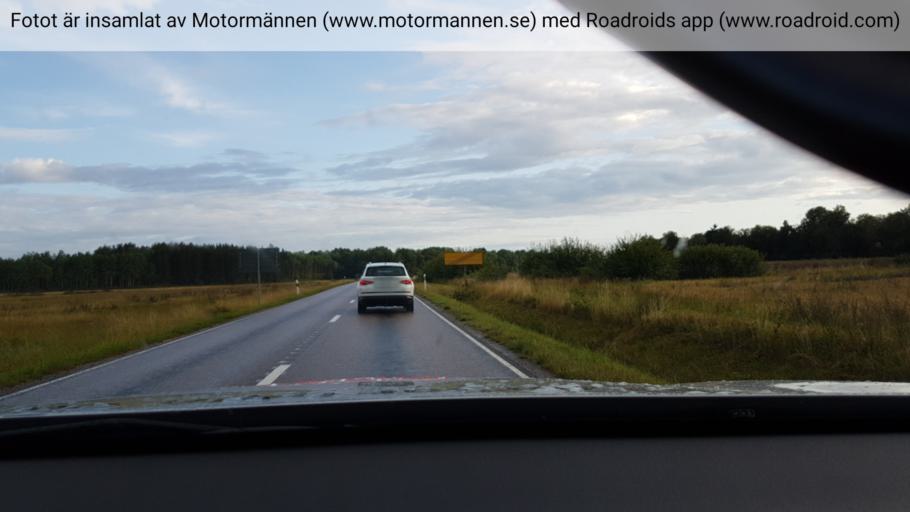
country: SE
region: Stockholm
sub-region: Norrtalje Kommun
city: Norrtalje
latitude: 59.8260
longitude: 18.6546
